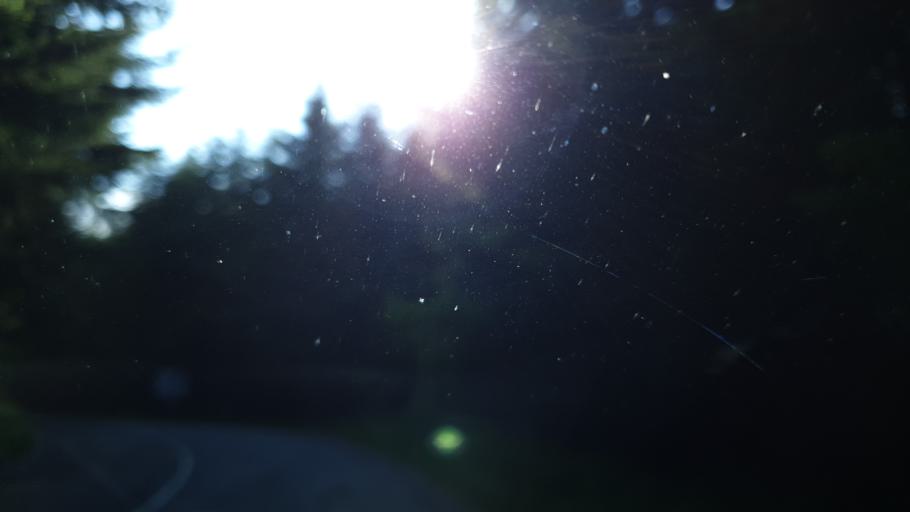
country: IT
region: Tuscany
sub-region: Province of Arezzo
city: Montemignaio
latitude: 43.7861
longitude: 11.6122
